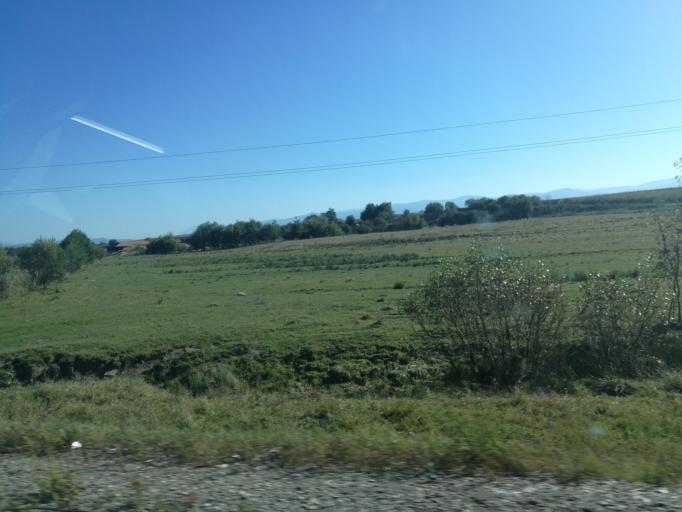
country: RO
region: Brasov
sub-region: Comuna Sercaia
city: Sercaia
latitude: 45.8246
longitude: 25.0939
